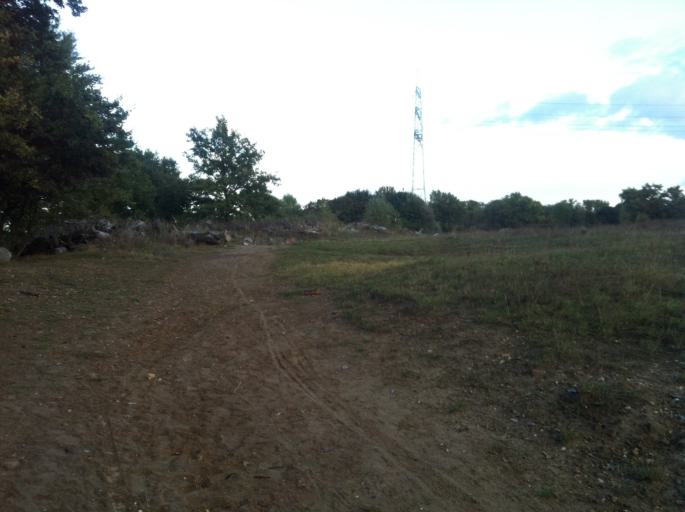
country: DE
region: Rheinland-Pfalz
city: Budenheim
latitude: 50.0197
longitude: 8.2047
